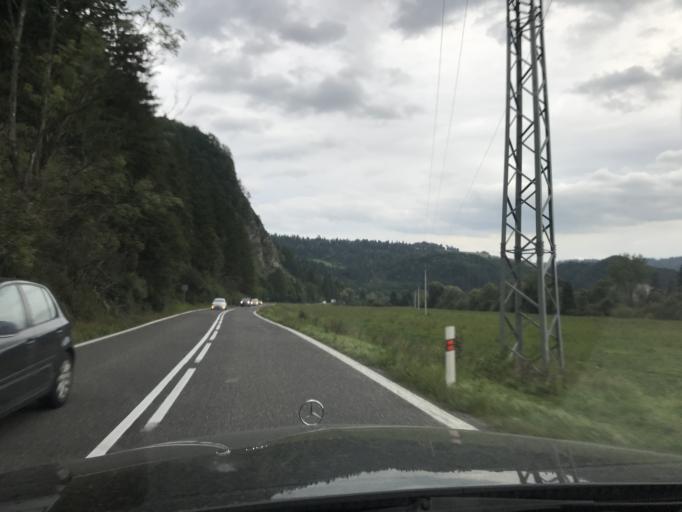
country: SK
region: Zilinsky
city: Tvrdosin
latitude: 49.2984
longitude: 19.4855
